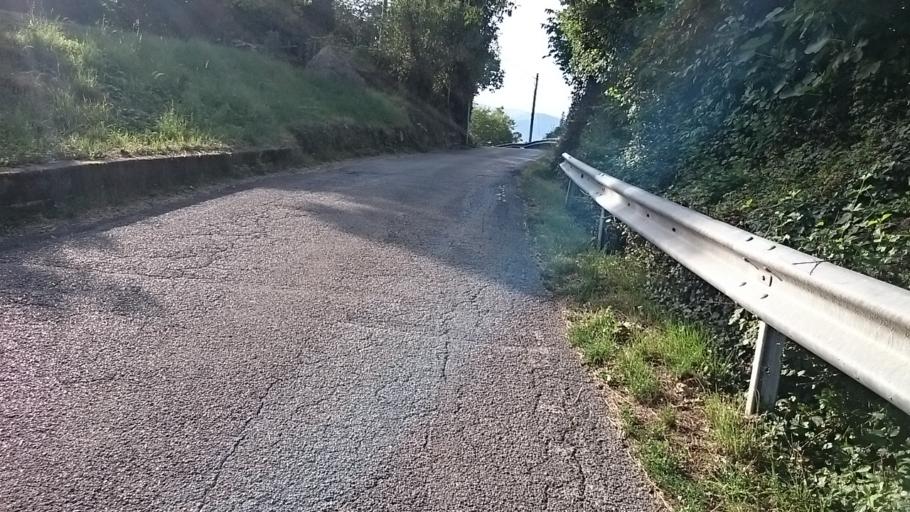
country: IT
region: Veneto
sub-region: Provincia di Treviso
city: Monfumo
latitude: 45.8468
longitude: 11.9224
